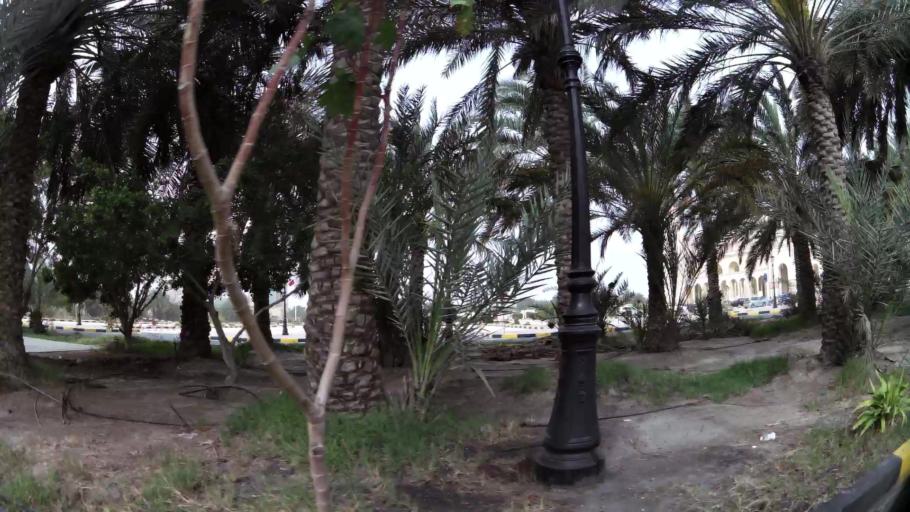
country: BH
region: Manama
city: Manama
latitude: 26.2178
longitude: 50.5995
